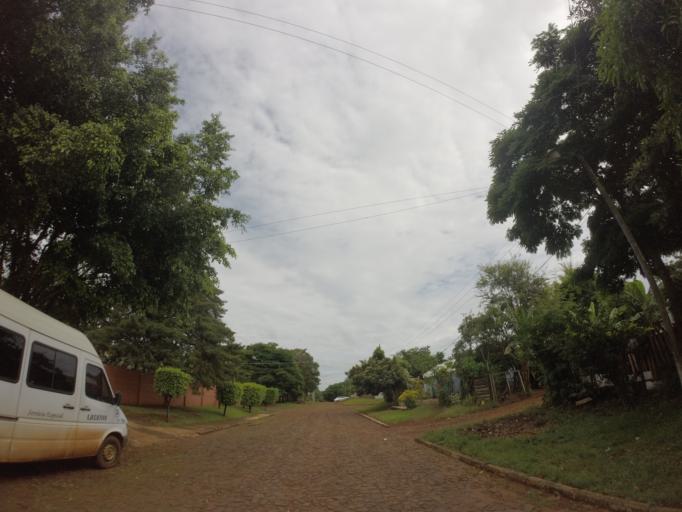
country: PY
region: Alto Parana
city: Ciudad del Este
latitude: -25.4052
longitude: -54.6487
